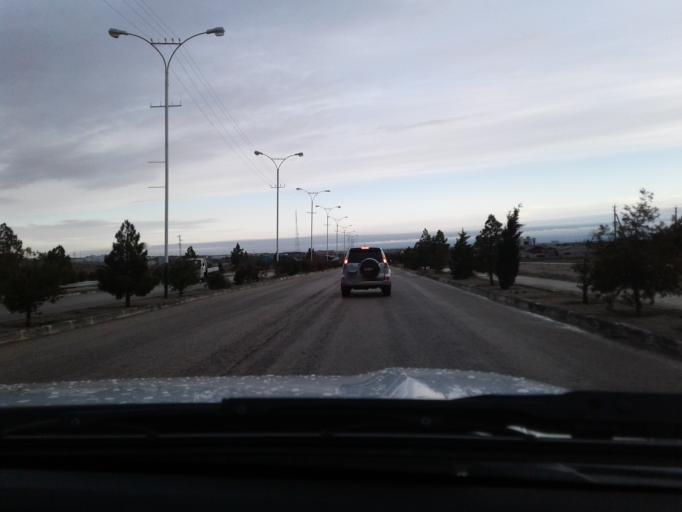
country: TM
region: Balkan
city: Balkanabat
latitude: 39.5349
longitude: 54.3522
